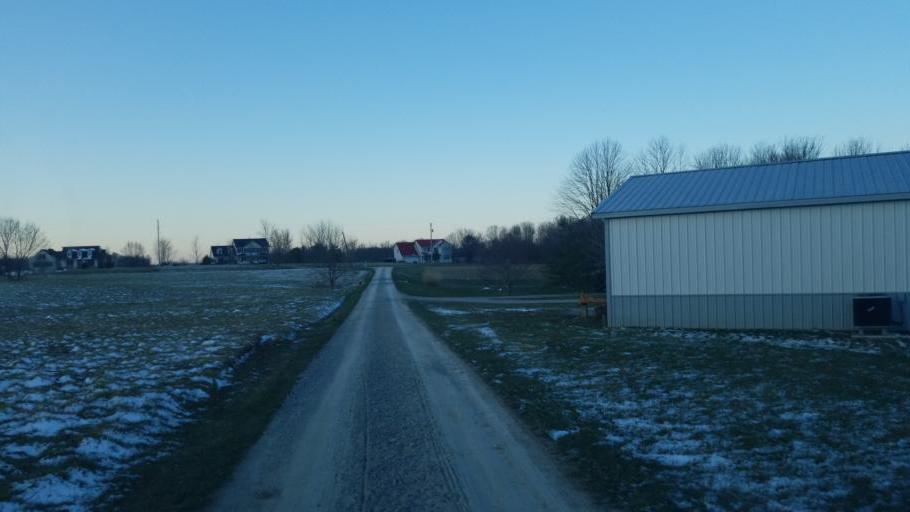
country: US
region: Ohio
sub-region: Highland County
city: Leesburg
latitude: 39.2849
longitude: -83.5189
